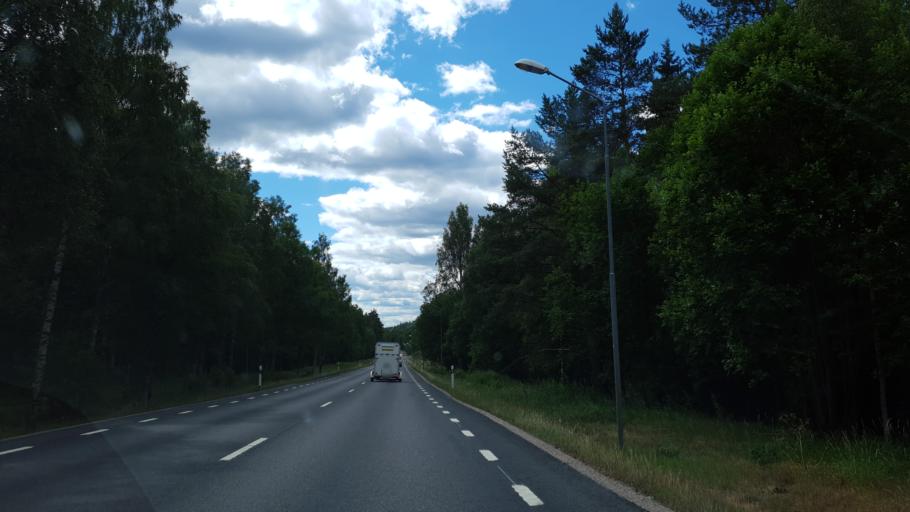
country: SE
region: Kronoberg
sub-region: Vaxjo Kommun
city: Braas
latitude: 57.2240
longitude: 15.1445
